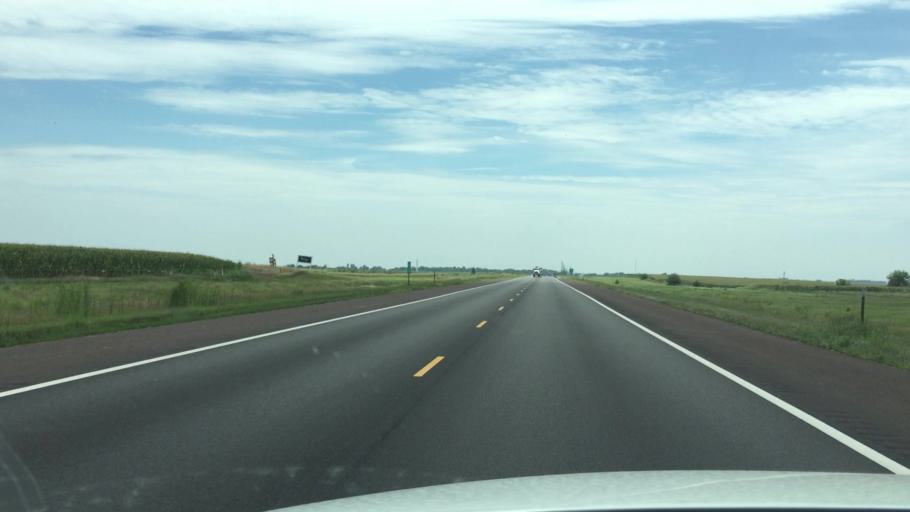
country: US
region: Kansas
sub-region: Nemaha County
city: Sabetha
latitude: 39.8547
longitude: -95.7533
